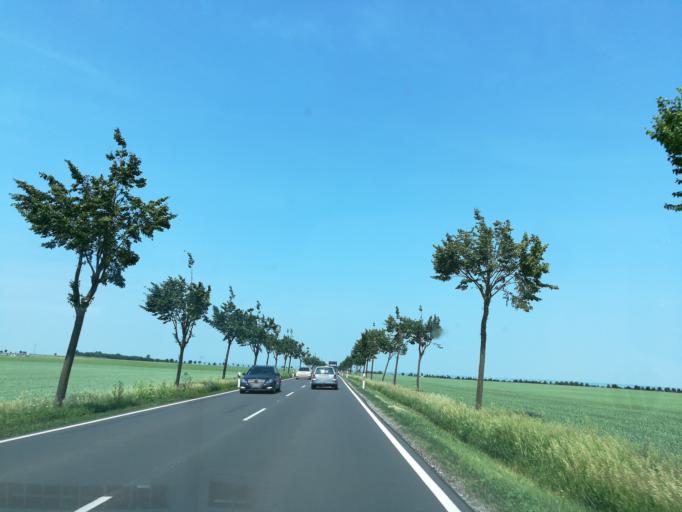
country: DE
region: Saxony-Anhalt
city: Gross Bornecke
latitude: 51.8512
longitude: 11.4527
